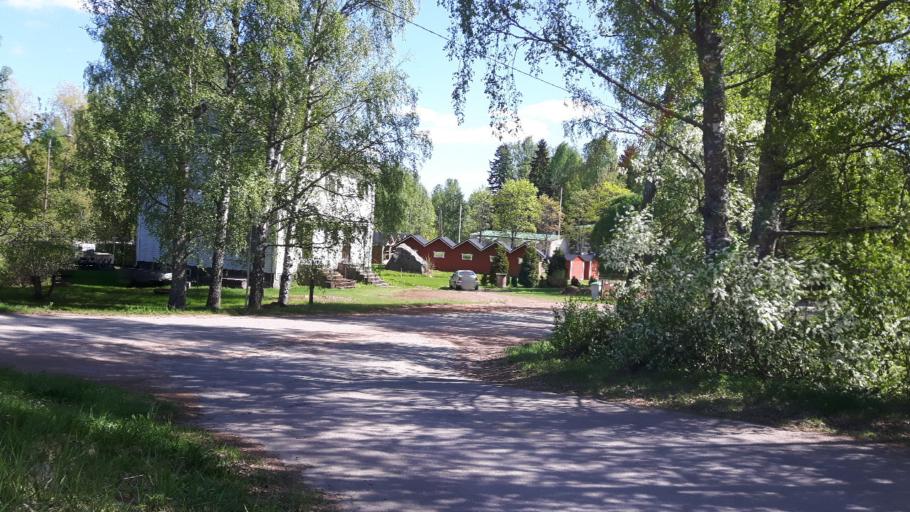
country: FI
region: Kymenlaakso
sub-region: Kotka-Hamina
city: Virolahti
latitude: 60.5163
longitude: 27.4622
